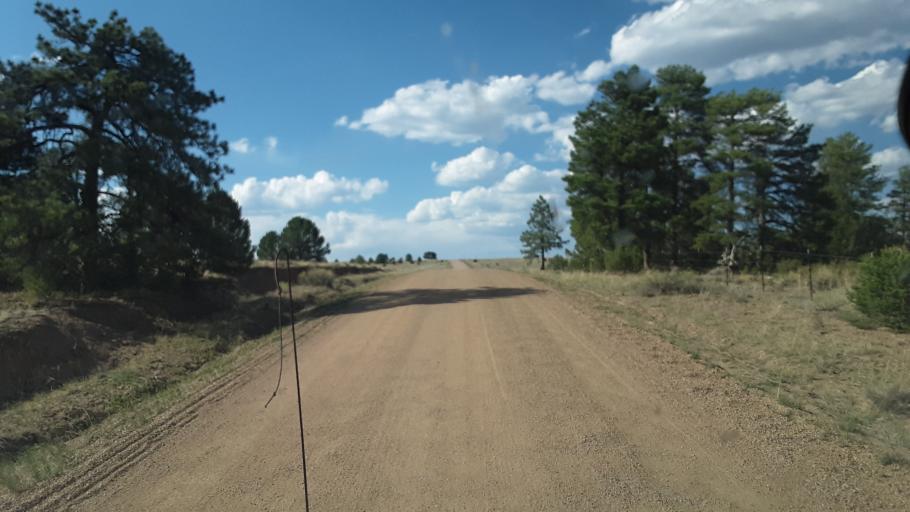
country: US
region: Colorado
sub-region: Custer County
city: Westcliffe
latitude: 38.2853
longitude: -105.4774
